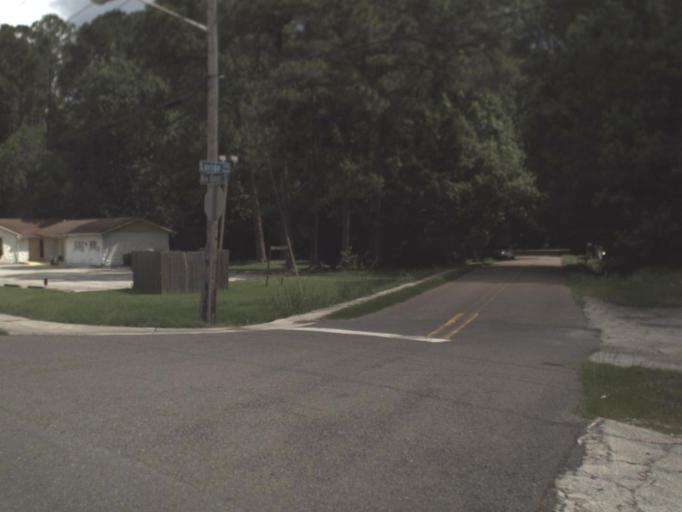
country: US
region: Florida
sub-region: Duval County
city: Jacksonville
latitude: 30.3900
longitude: -81.7350
